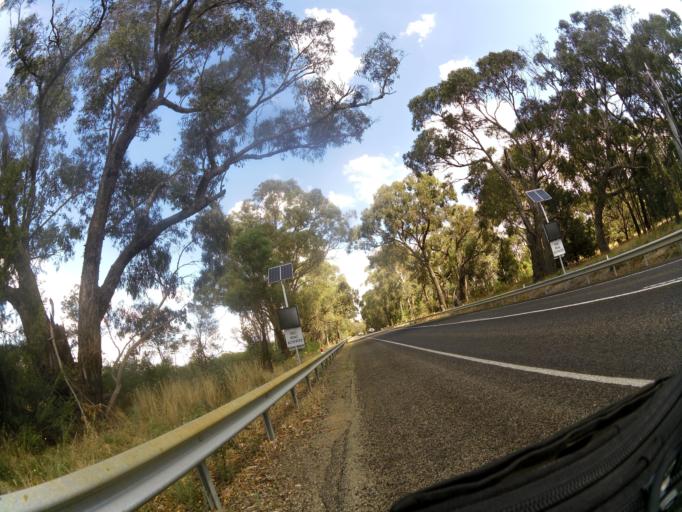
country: AU
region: Victoria
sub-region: Mansfield
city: Mansfield
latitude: -36.8340
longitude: 146.0079
